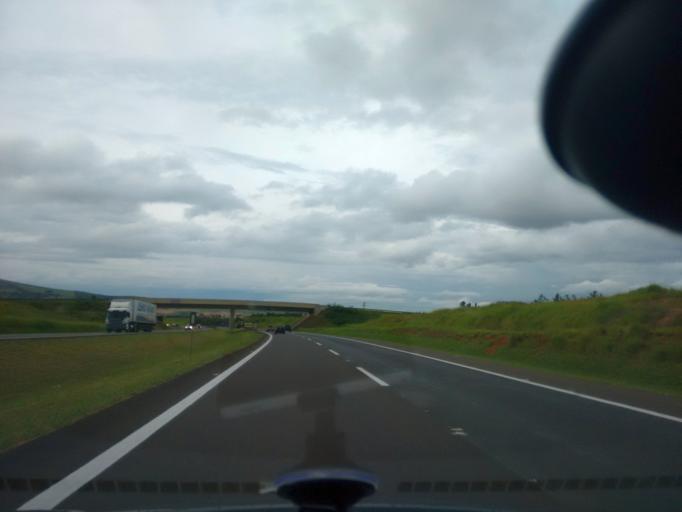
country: BR
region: Sao Paulo
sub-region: Limeira
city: Limeira
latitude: -22.5722
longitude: -47.4576
